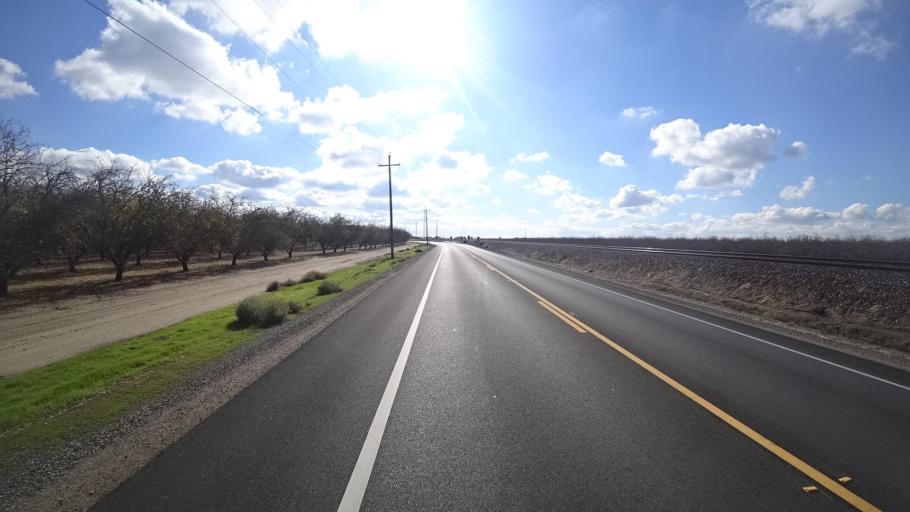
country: US
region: California
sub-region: Kern County
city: Wasco
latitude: 35.6840
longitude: -119.3305
